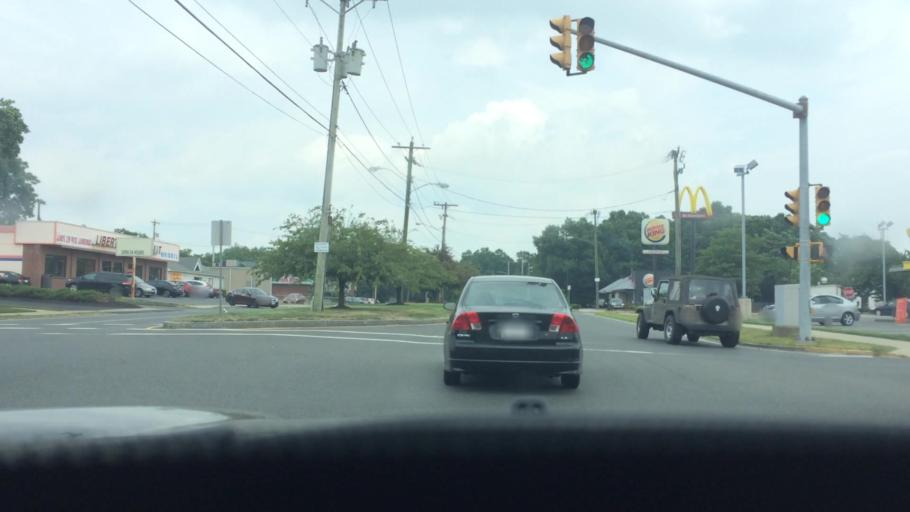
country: US
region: Massachusetts
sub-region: Hampden County
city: Chicopee
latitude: 42.1390
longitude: -72.5825
